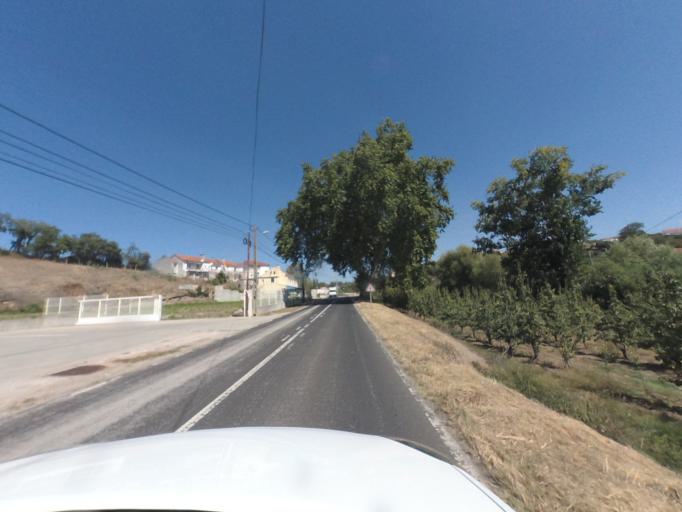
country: PT
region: Leiria
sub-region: Alcobaca
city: Alcobaca
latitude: 39.5248
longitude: -9.0015
